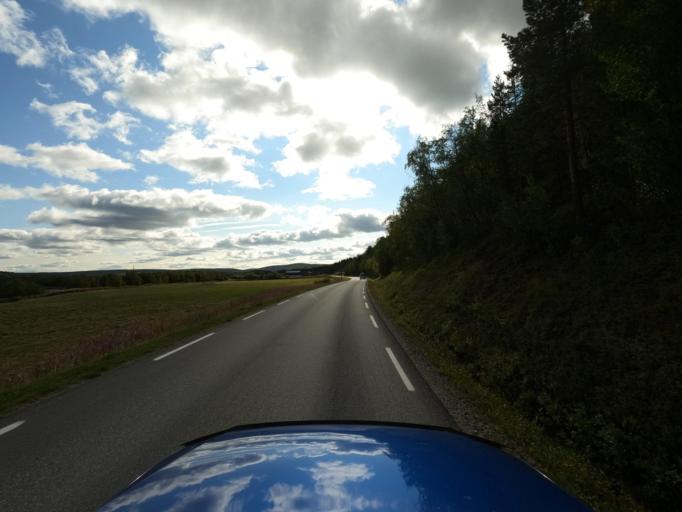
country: NO
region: Finnmark Fylke
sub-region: Karasjok
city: Karasjohka
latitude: 69.4096
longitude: 25.8059
